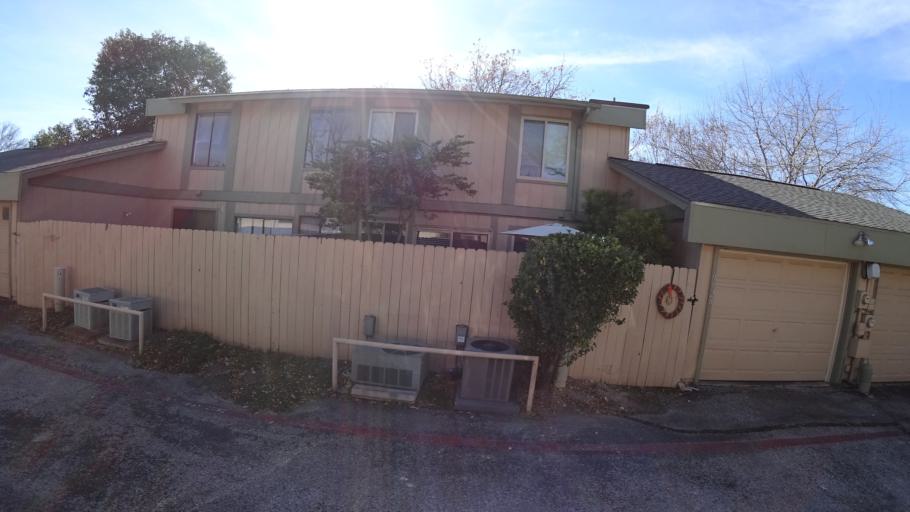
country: US
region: Texas
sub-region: Travis County
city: Wells Branch
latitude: 30.3672
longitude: -97.6981
